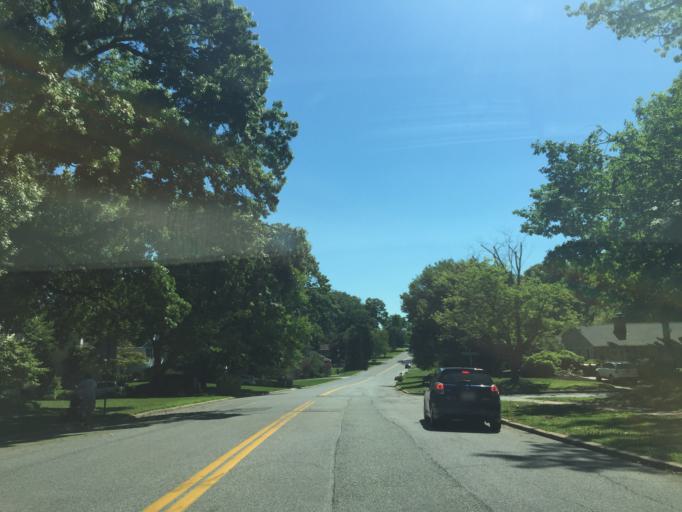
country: US
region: Maryland
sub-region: Baltimore County
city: Timonium
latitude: 39.4327
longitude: -76.6122
